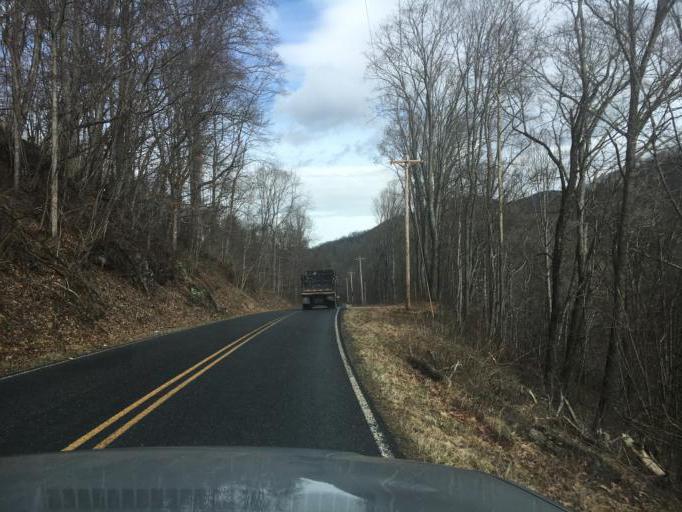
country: US
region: North Carolina
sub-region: Haywood County
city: Canton
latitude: 35.3876
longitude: -82.8150
